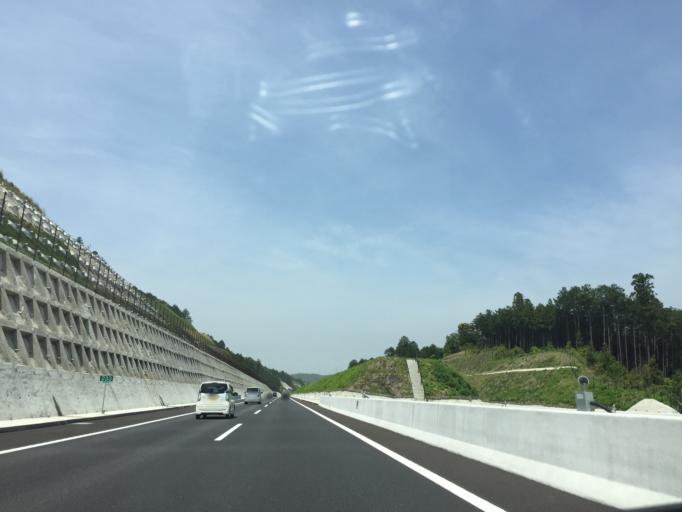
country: JP
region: Aichi
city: Gamagori
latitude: 34.9036
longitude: 137.3094
